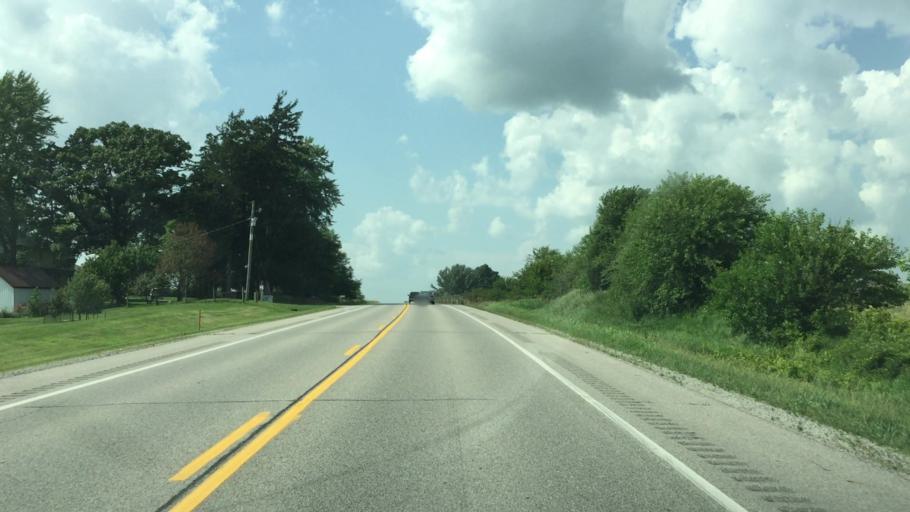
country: US
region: Iowa
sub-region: Johnson County
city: Solon
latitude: 41.7598
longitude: -91.4784
